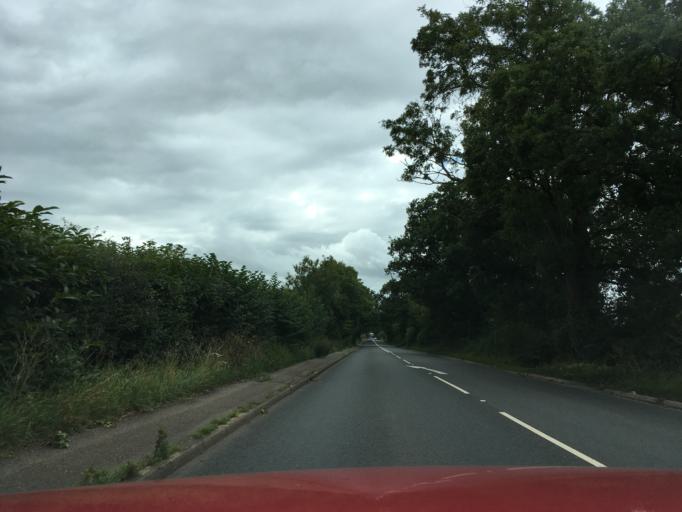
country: GB
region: England
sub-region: Devon
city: Uffculme
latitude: 50.9140
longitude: -3.3474
